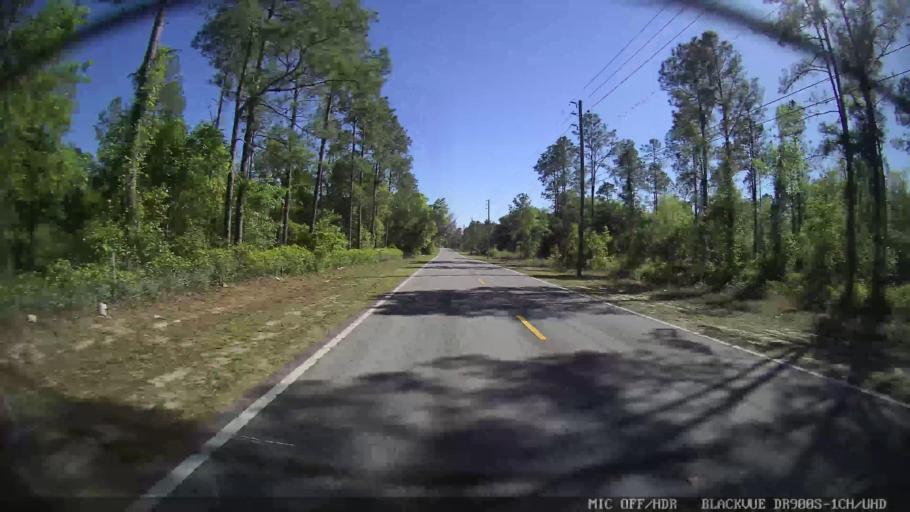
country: US
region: Florida
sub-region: Pasco County
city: Shady Hills
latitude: 28.3544
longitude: -82.5426
